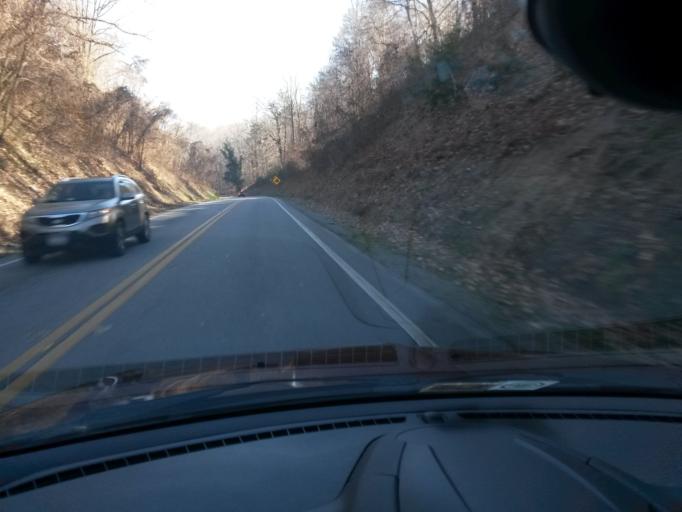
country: US
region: Virginia
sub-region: Henry County
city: Bassett
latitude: 36.7606
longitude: -80.0186
